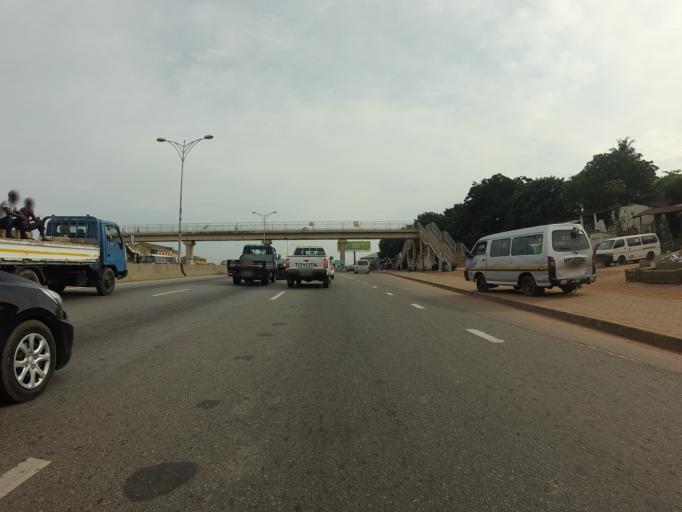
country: GH
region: Greater Accra
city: Gbawe
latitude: 5.5889
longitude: -0.2707
